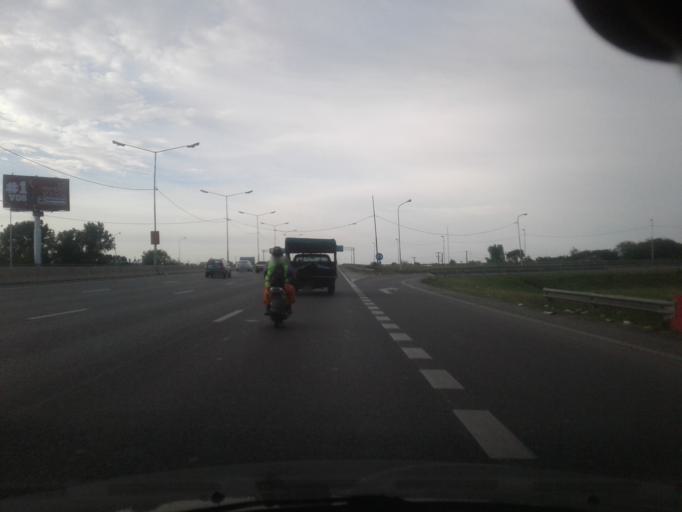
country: AR
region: Santa Fe
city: Perez
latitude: -32.9490
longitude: -60.7222
